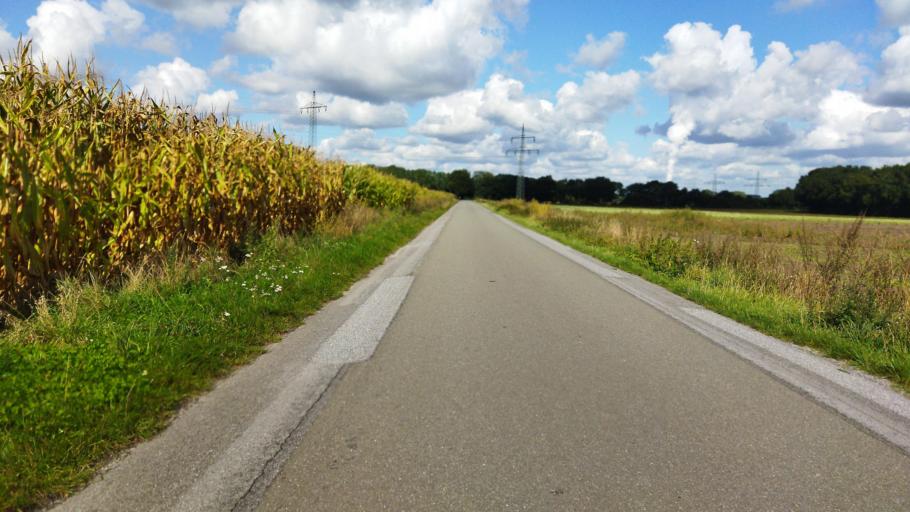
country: DE
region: Lower Saxony
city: Emsburen
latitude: 52.3886
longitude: 7.3270
